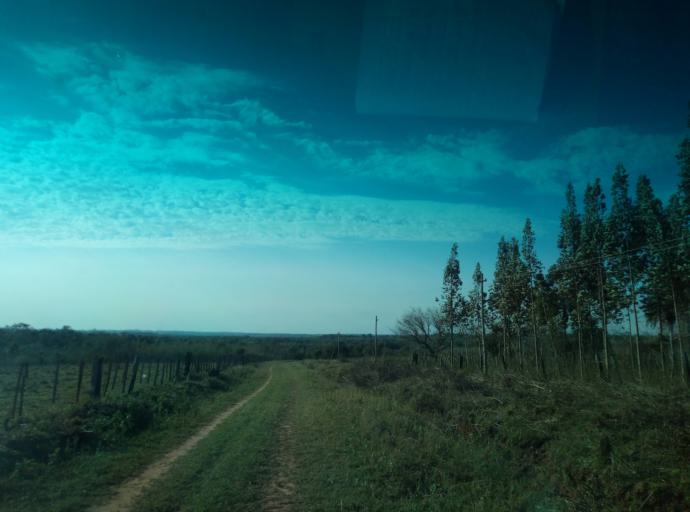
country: PY
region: Caaguazu
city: Doctor Cecilio Baez
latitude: -25.1606
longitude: -56.2320
